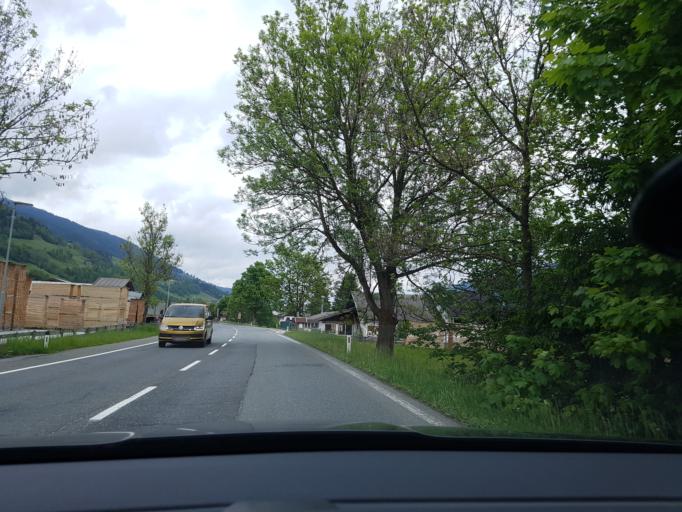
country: AT
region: Salzburg
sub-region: Politischer Bezirk Zell am See
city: Stuhlfelden
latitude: 47.2865
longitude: 12.5310
